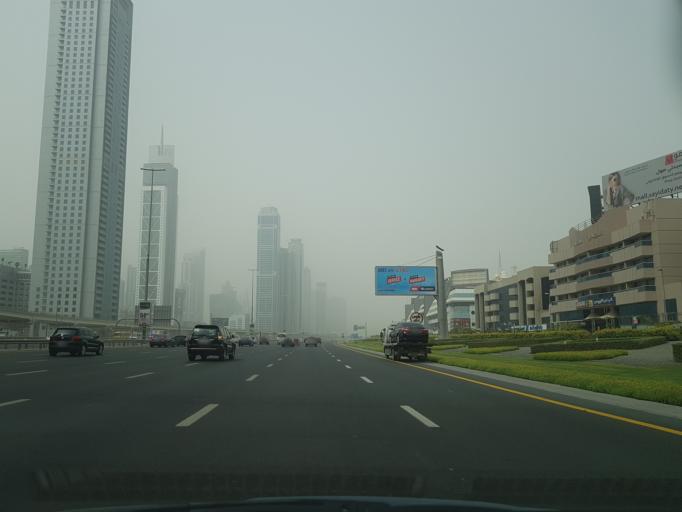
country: AE
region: Dubai
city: Dubai
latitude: 25.2008
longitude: 55.2678
